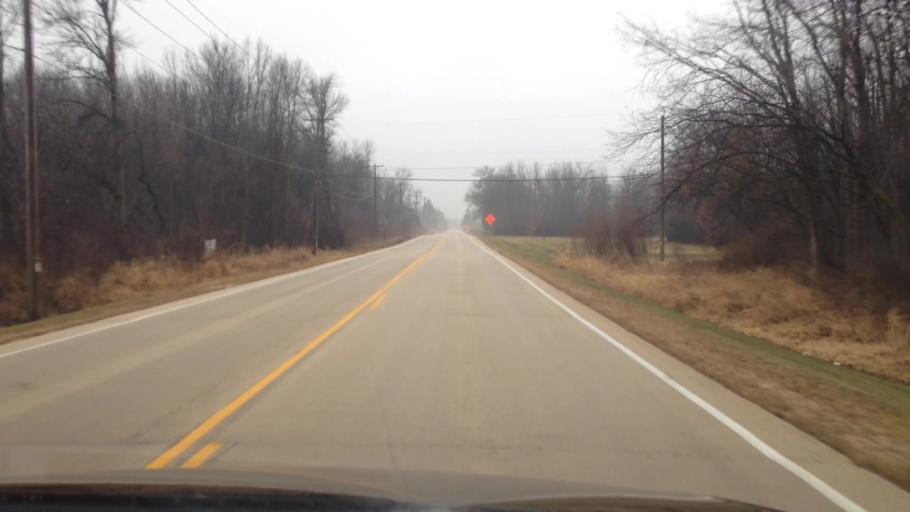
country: US
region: Wisconsin
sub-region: Washington County
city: Richfield
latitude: 43.2280
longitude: -88.1623
